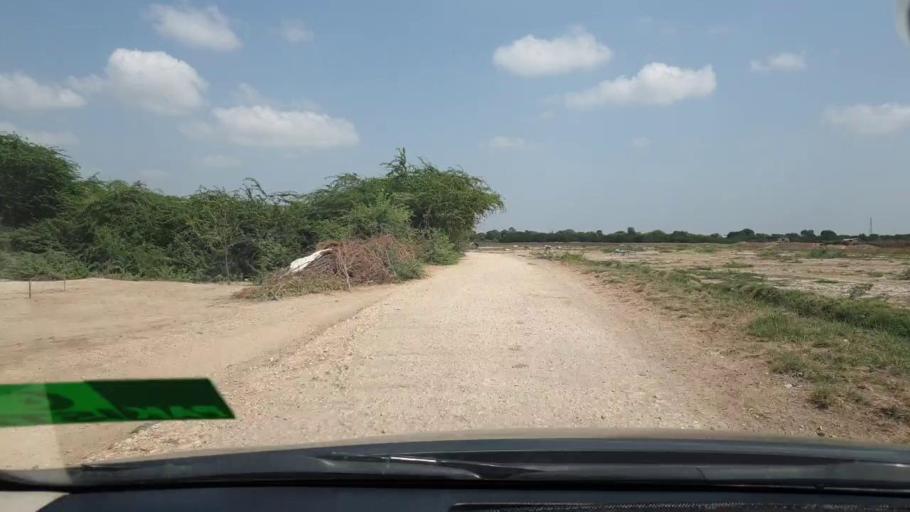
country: PK
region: Sindh
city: Naukot
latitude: 24.8834
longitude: 69.2379
